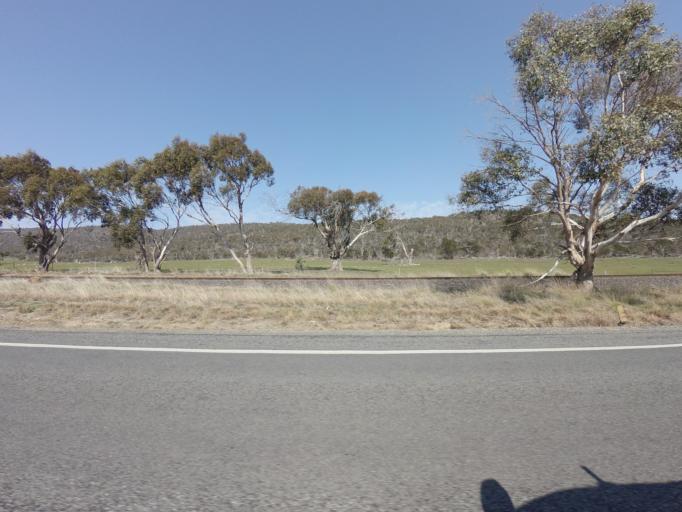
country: AU
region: Tasmania
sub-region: Northern Midlands
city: Evandale
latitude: -41.8101
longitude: 147.6002
